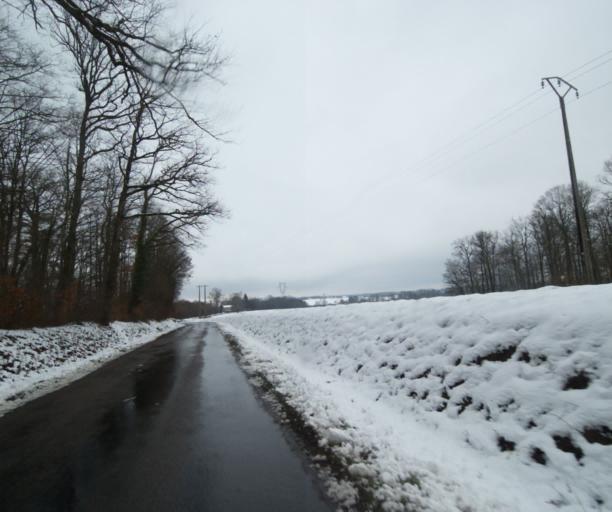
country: FR
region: Champagne-Ardenne
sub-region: Departement de la Haute-Marne
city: Laneuville-a-Remy
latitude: 48.5166
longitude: 4.8400
